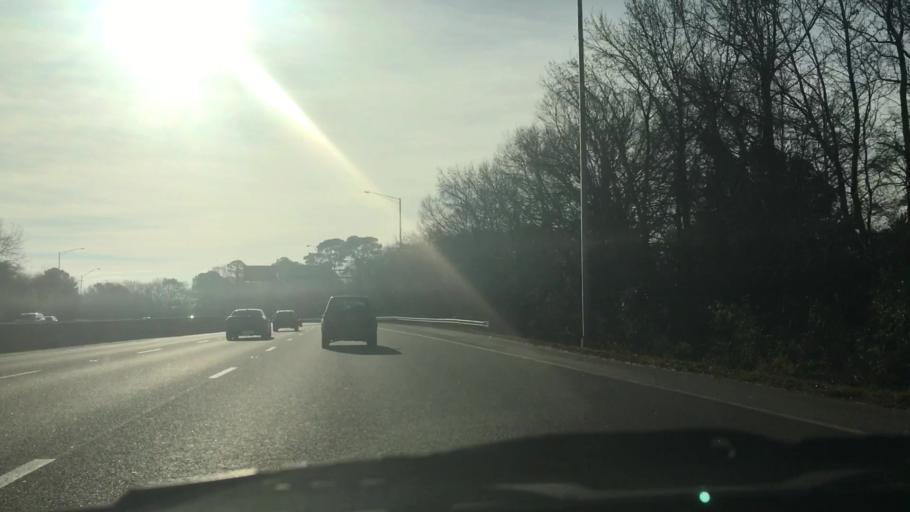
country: US
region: Virginia
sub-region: City of Norfolk
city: Norfolk
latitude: 36.8883
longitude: -76.2292
